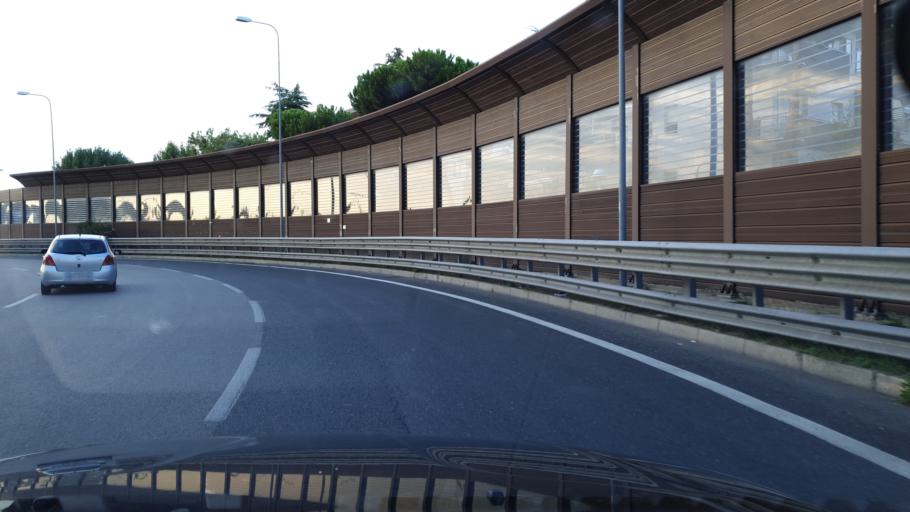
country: IT
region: Emilia-Romagna
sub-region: Provincia di Rimini
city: Rivazzurra
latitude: 44.0408
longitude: 12.5916
